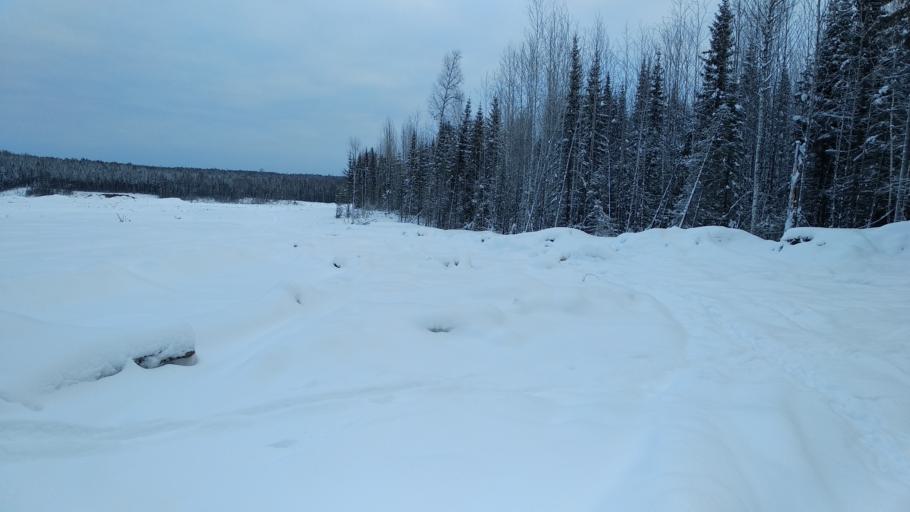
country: RU
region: Sverdlovsk
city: Krasnotur'insk
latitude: 59.6878
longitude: 60.1377
